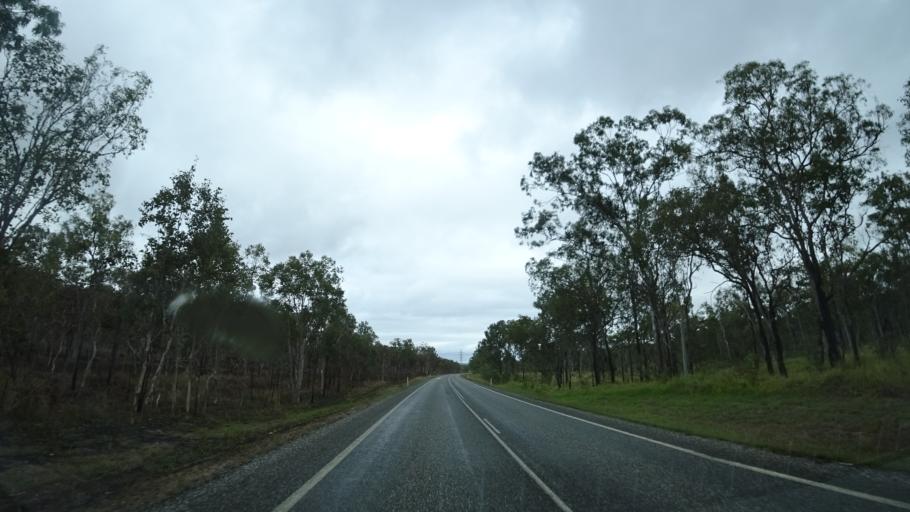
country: AU
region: Queensland
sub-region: Tablelands
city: Mareeba
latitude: -16.7354
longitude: 145.3507
